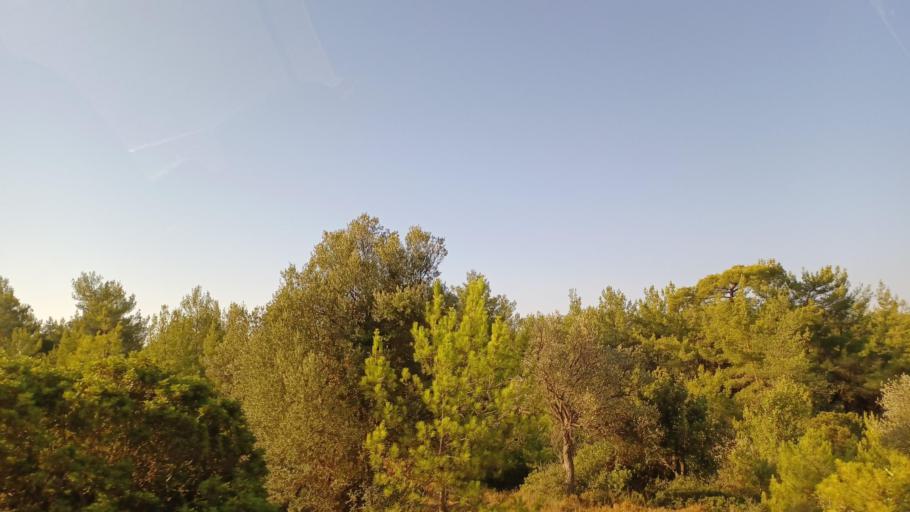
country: CY
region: Limassol
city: Pissouri
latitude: 34.7279
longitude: 32.6782
